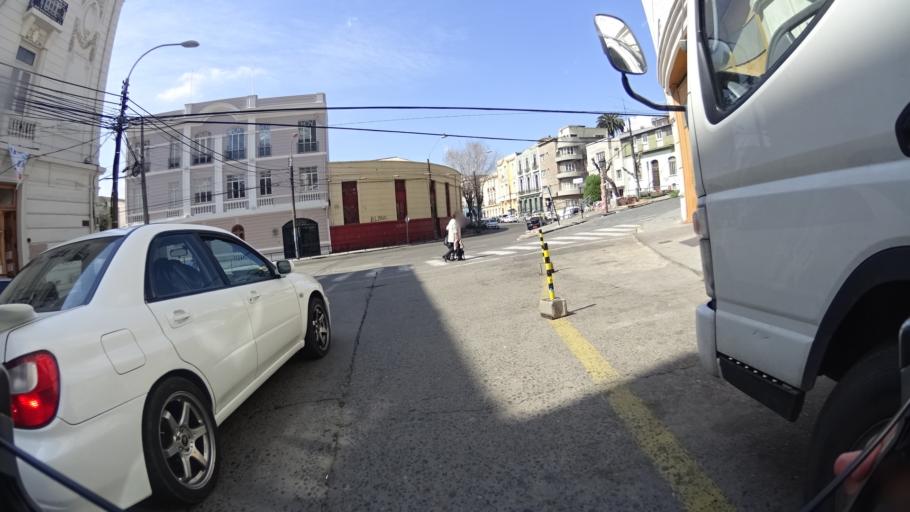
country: CL
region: Valparaiso
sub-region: Provincia de Valparaiso
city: Valparaiso
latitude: -33.0472
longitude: -71.6194
